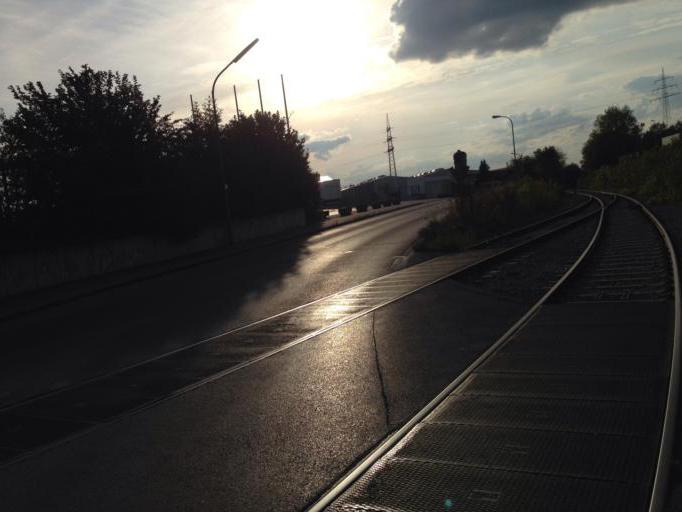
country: DE
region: Bavaria
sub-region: Swabia
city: Augsburg
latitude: 48.3426
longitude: 10.8933
